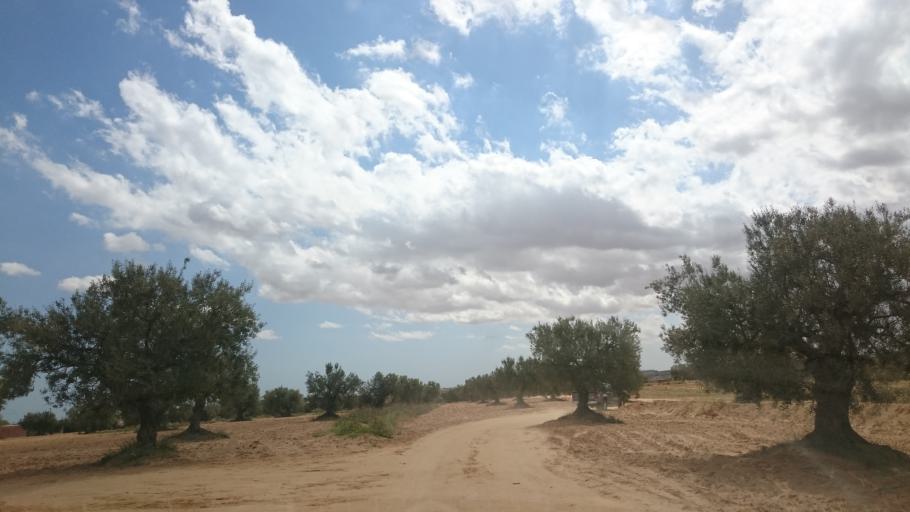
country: TN
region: Safaqis
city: Sfax
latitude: 34.7499
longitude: 10.4873
